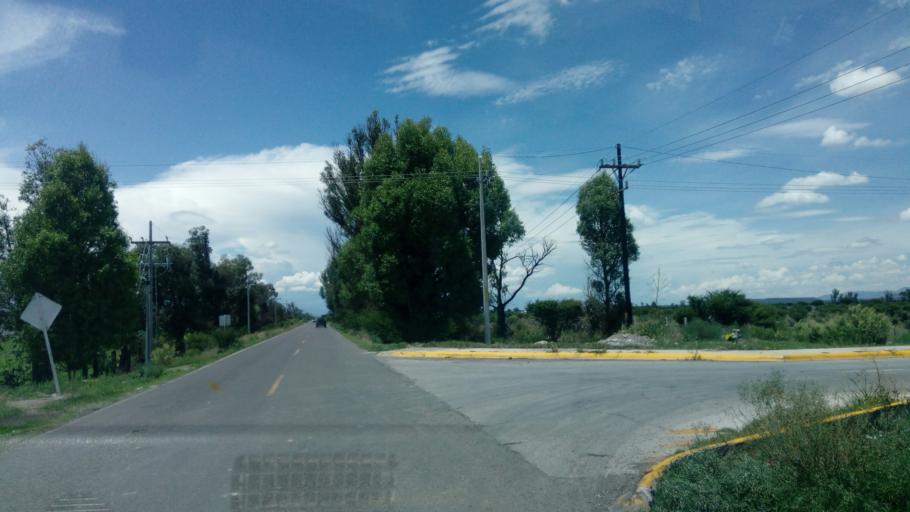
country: MX
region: Durango
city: Victoria de Durango
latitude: 24.1600
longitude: -104.5211
